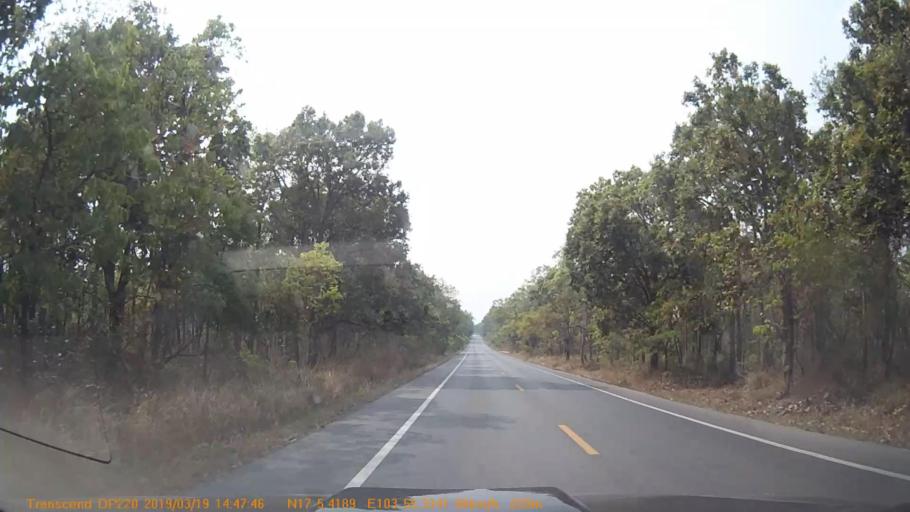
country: TH
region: Sakon Nakhon
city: Kut Bak
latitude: 17.0907
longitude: 103.9218
